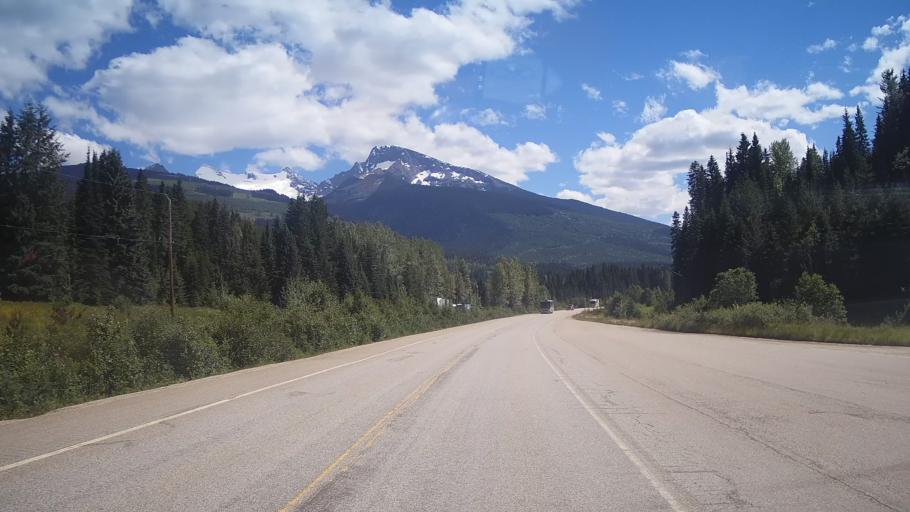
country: CA
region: Alberta
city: Jasper Park Lodge
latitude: 52.5864
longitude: -119.0958
